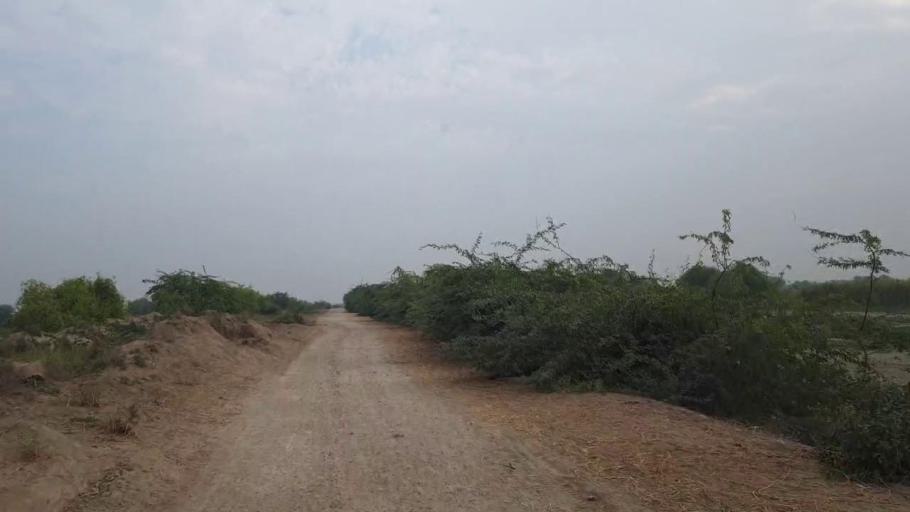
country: PK
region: Sindh
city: Talhar
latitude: 24.8086
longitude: 68.8730
